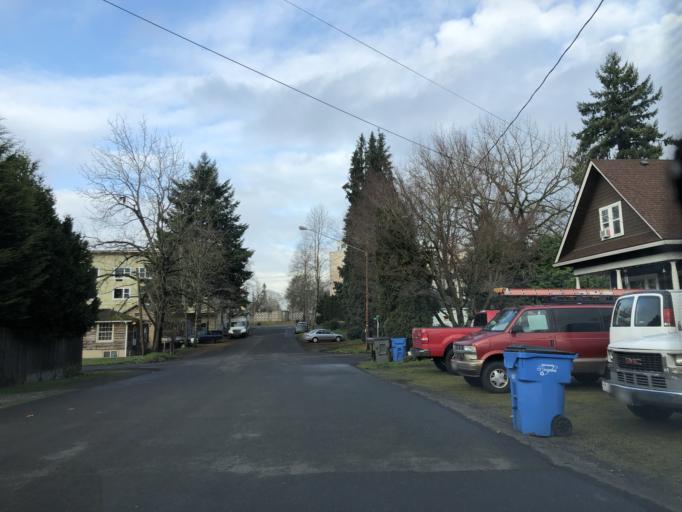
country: US
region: Washington
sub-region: Clark County
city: Vancouver
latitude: 45.6315
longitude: -122.6822
